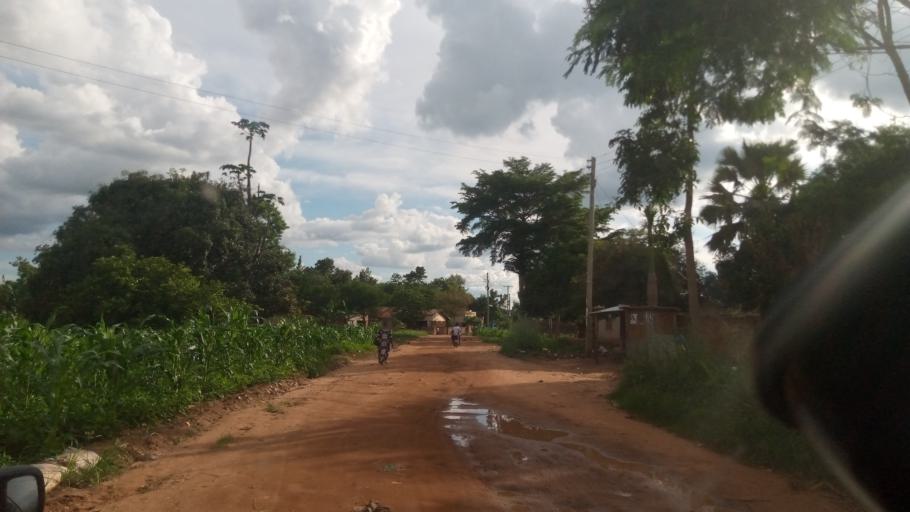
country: UG
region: Northern Region
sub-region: Lira District
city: Lira
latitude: 2.2267
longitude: 32.8919
